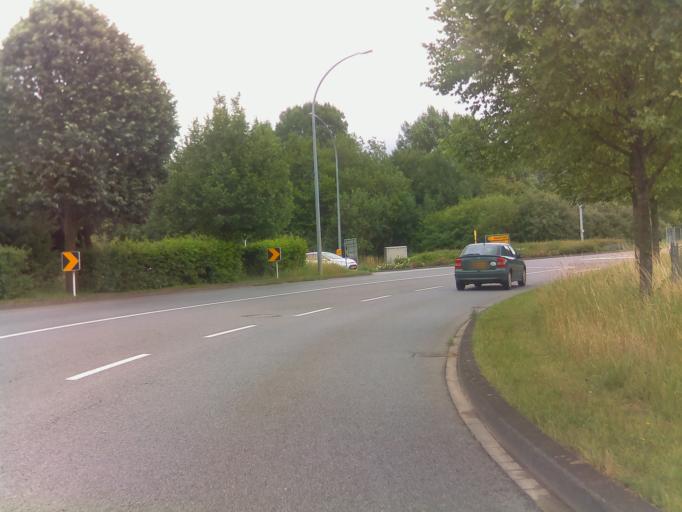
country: LU
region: Luxembourg
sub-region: Canton d'Esch-sur-Alzette
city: Bettembourg
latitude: 49.5211
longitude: 6.0891
